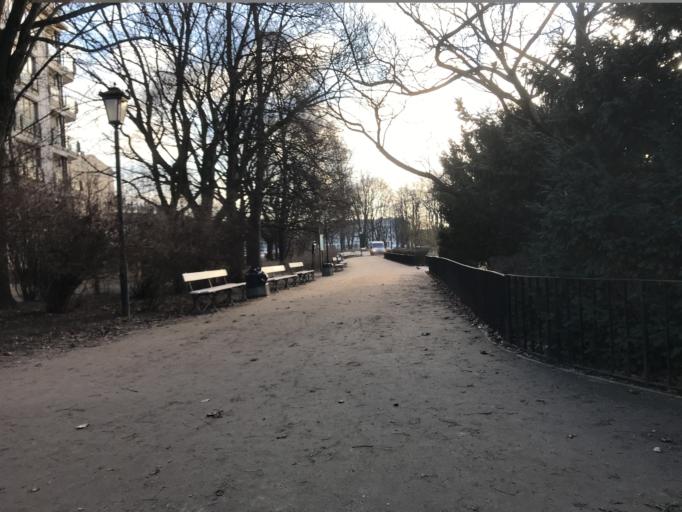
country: PL
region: Masovian Voivodeship
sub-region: Warszawa
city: Warsaw
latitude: 52.2416
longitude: 21.0077
